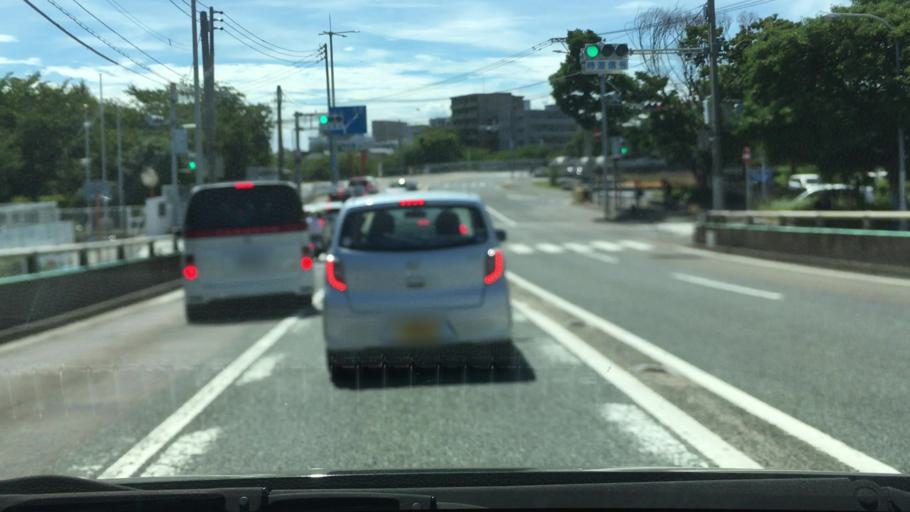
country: JP
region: Fukuoka
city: Fukuoka-shi
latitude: 33.5756
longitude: 130.4212
